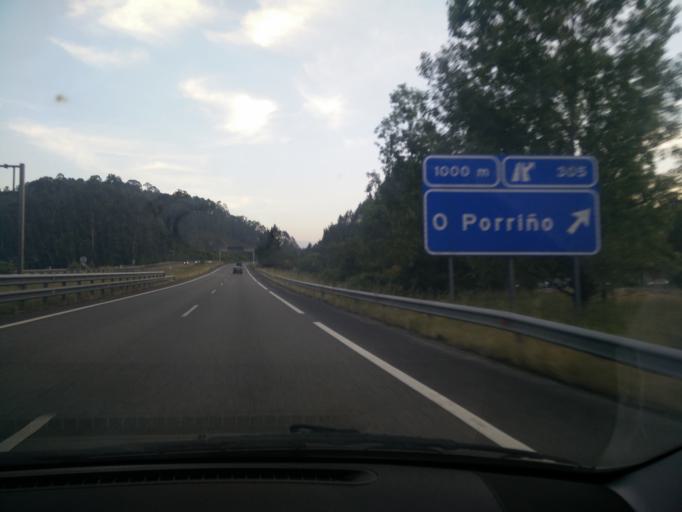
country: ES
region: Galicia
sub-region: Provincia de Pontevedra
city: Porrino
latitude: 42.1639
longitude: -8.5971
